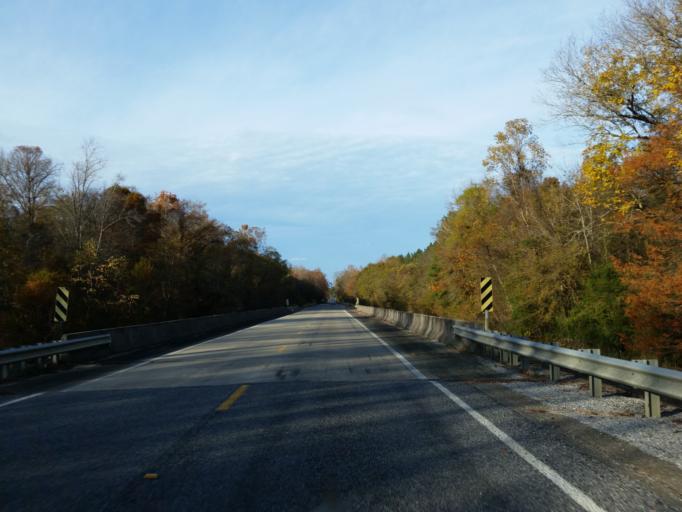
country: US
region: Mississippi
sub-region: Clarke County
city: Stonewall
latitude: 32.0567
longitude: -88.8810
